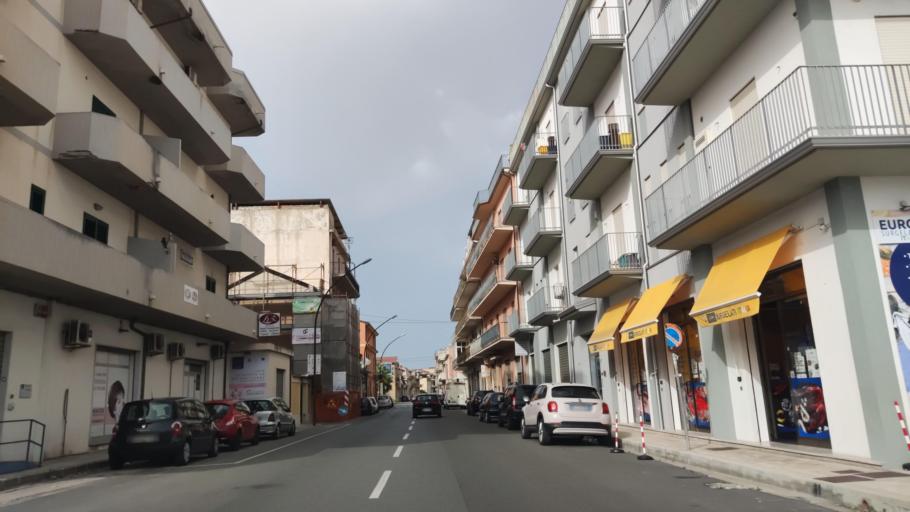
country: IT
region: Calabria
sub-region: Provincia di Reggio Calabria
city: Siderno
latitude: 38.2600
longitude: 16.2874
